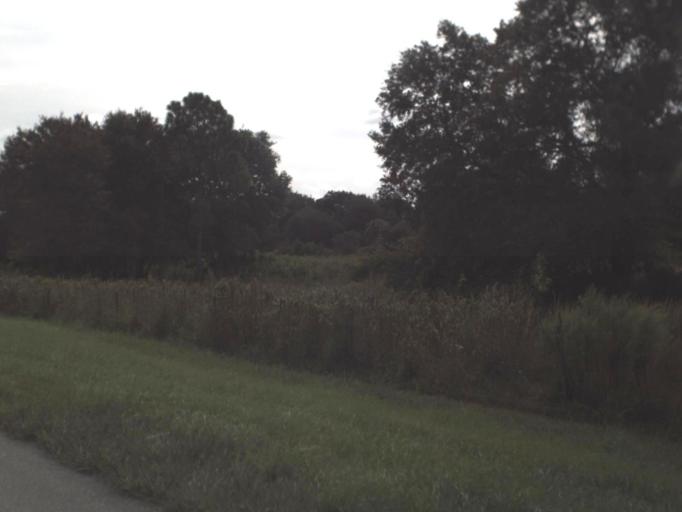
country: US
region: Florida
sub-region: Highlands County
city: Placid Lakes
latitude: 27.2092
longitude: -81.4643
